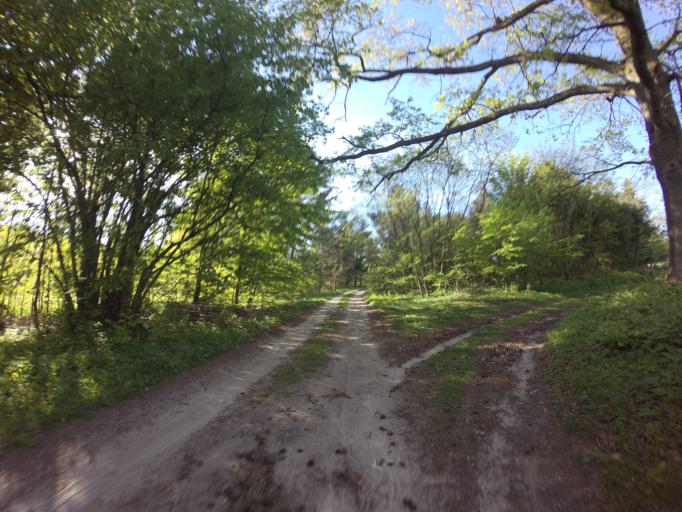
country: PL
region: West Pomeranian Voivodeship
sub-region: Powiat choszczenski
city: Drawno
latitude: 53.2124
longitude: 15.7287
